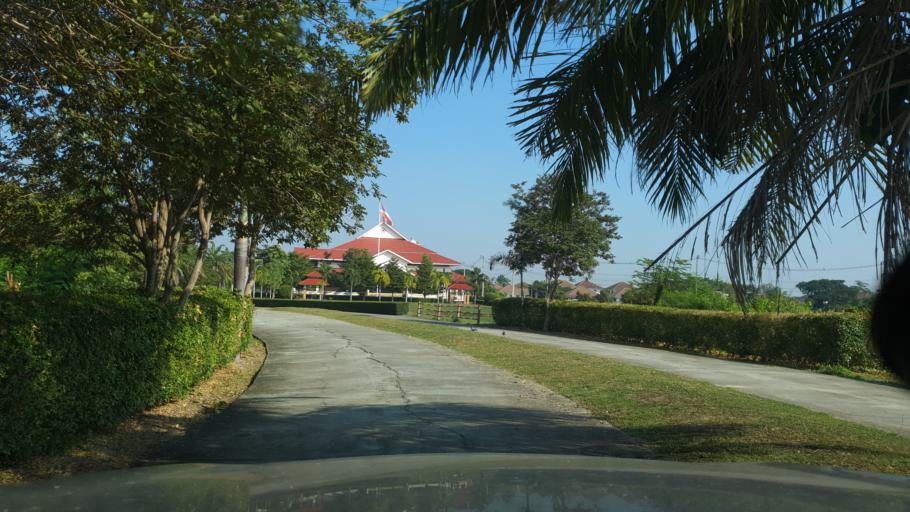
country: TH
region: Chiang Mai
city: Saraphi
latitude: 18.7100
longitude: 98.9752
